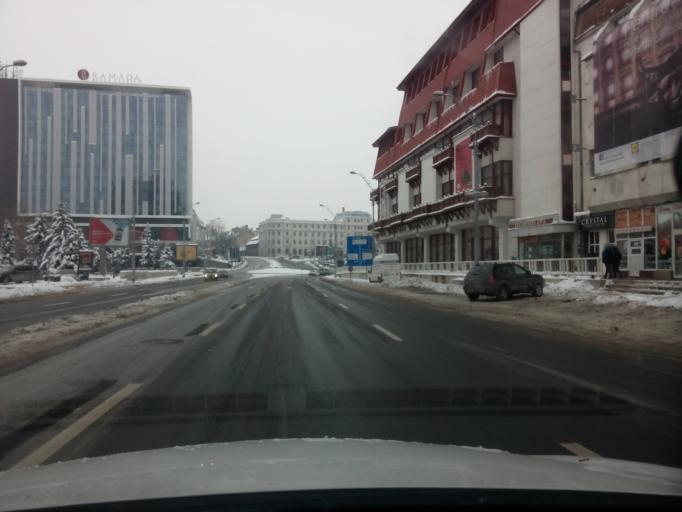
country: RO
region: Sibiu
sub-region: Municipiul Sibiu
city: Sibiu
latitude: 45.7898
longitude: 24.1496
